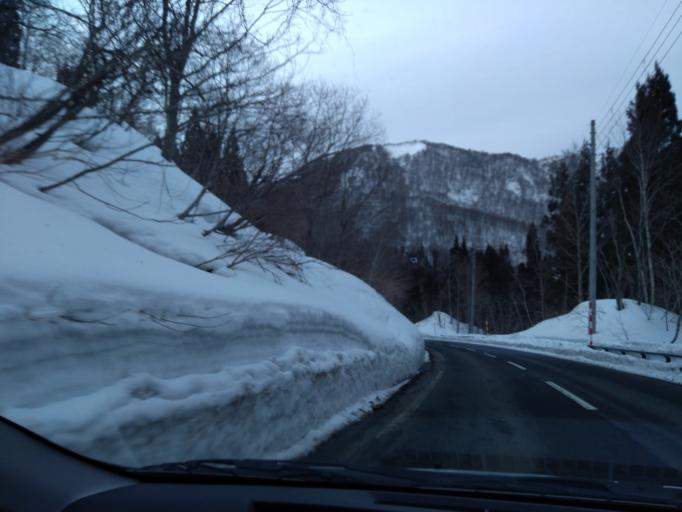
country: JP
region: Iwate
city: Kitakami
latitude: 39.2359
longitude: 140.9159
